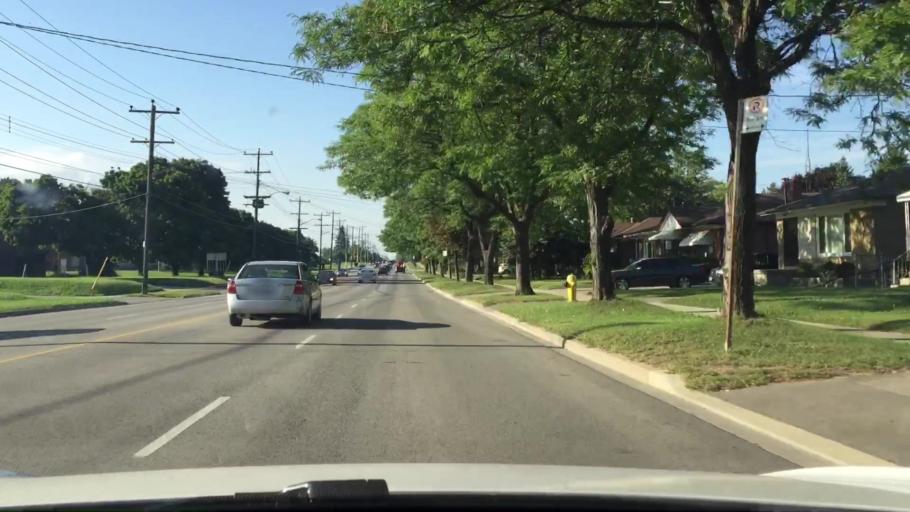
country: CA
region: Ontario
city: Scarborough
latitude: 43.7499
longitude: -79.2858
